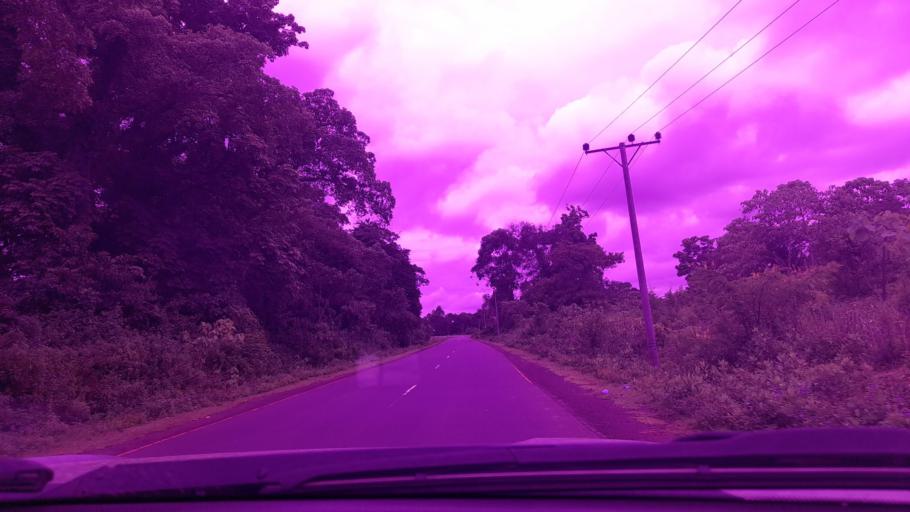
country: ET
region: Southern Nations, Nationalities, and People's Region
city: Bonga
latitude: 7.2825
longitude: 35.9599
